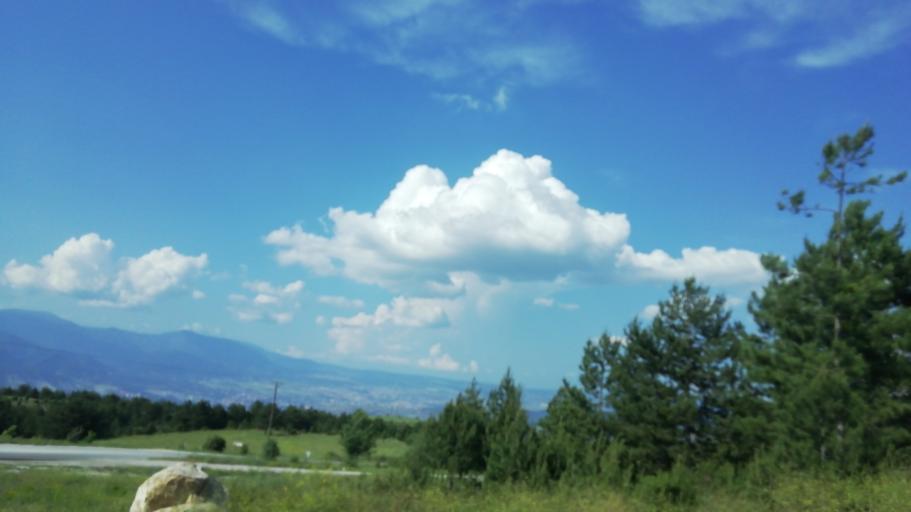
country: TR
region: Karabuk
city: Karabuk
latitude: 41.1272
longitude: 32.6049
